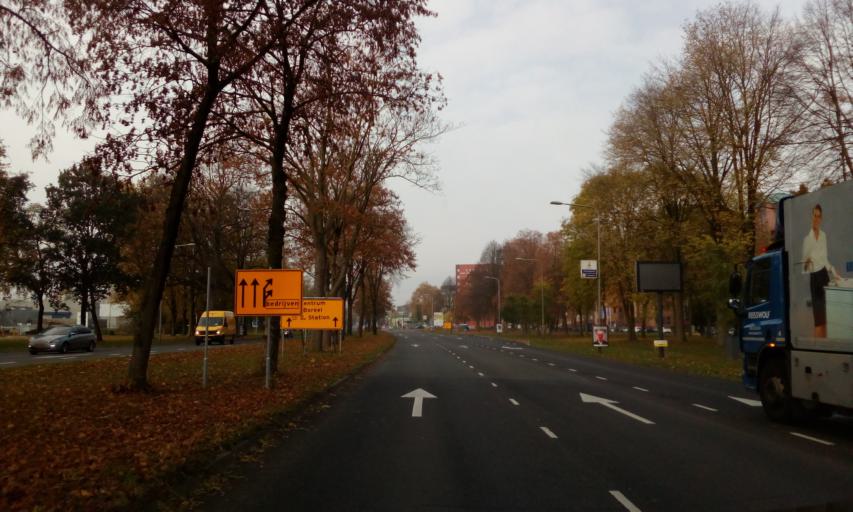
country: NL
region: Overijssel
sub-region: Gemeente Deventer
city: Deventer
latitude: 52.2398
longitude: 6.1762
